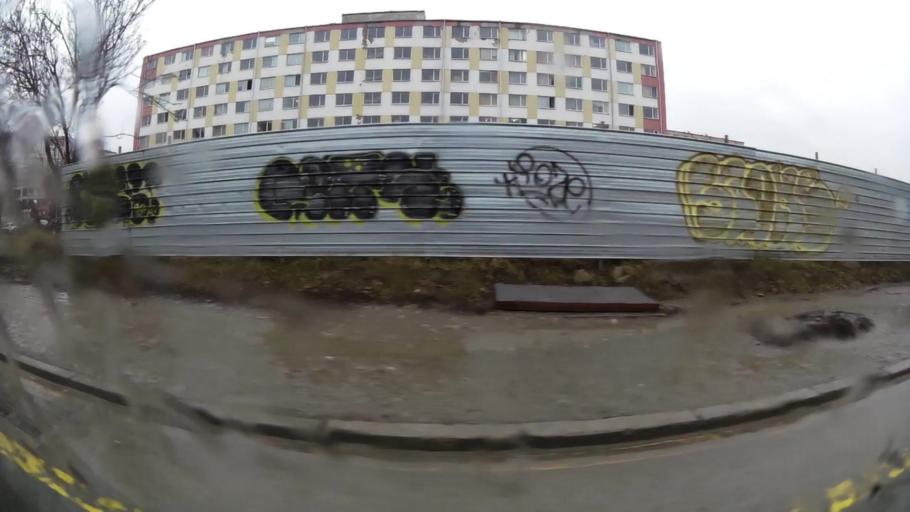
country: BG
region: Sofia-Capital
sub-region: Stolichna Obshtina
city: Sofia
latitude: 42.6584
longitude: 23.3486
